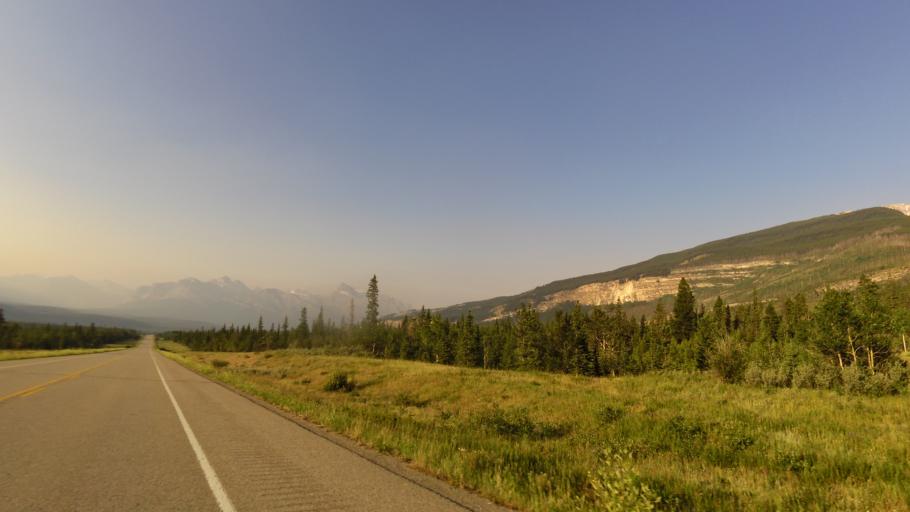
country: CA
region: Alberta
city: Lake Louise
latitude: 52.0740
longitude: -116.4190
